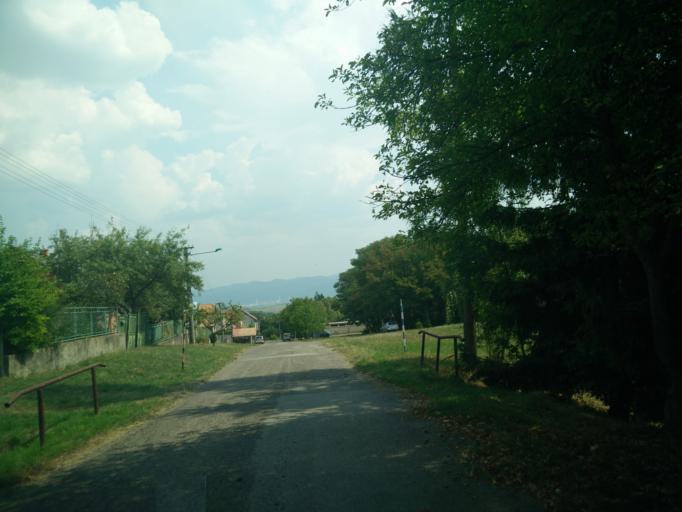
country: SK
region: Banskobystricky
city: Ziar nad Hronom
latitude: 48.5910
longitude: 18.7532
